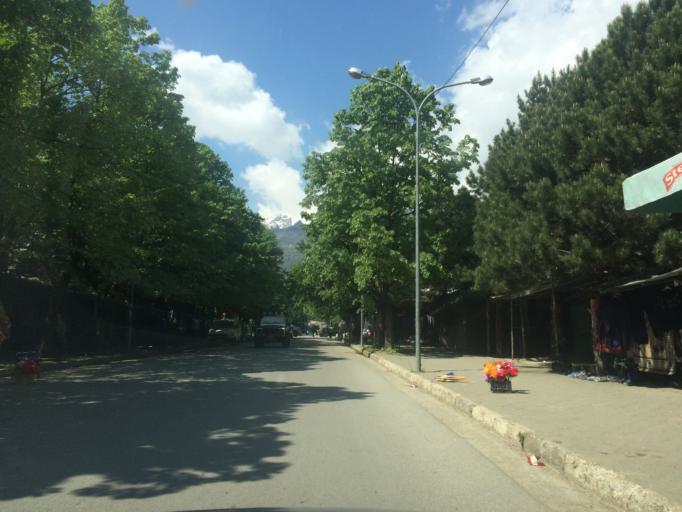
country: AL
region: Kukes
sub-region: Rrethi i Tropojes
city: Bajram Curri
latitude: 42.3570
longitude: 20.0783
